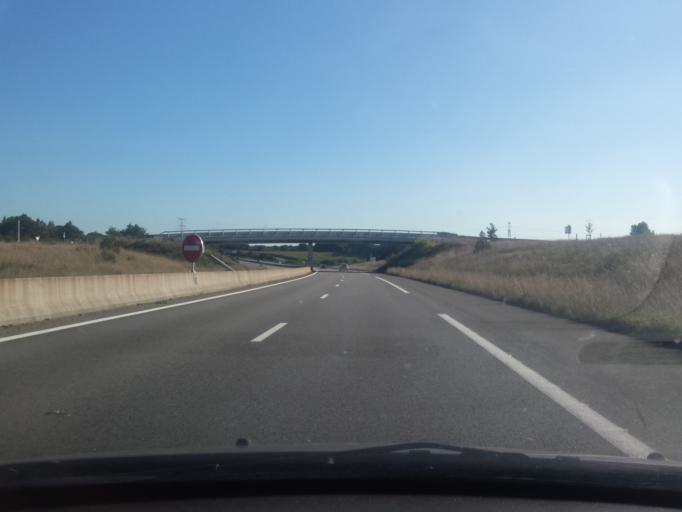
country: FR
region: Brittany
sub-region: Departement du Morbihan
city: Colpo
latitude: 47.7803
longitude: -2.7989
